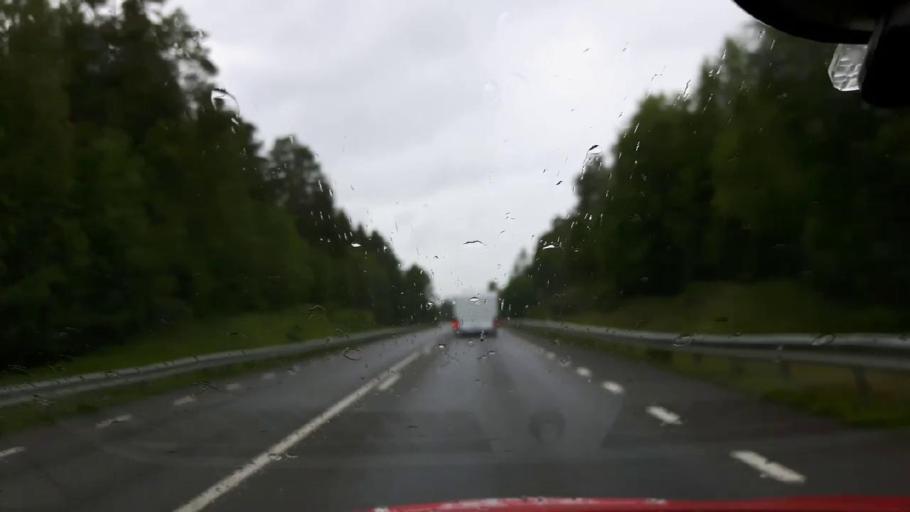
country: SE
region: Jaemtland
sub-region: Are Kommun
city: Jarpen
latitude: 63.3177
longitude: 13.5753
